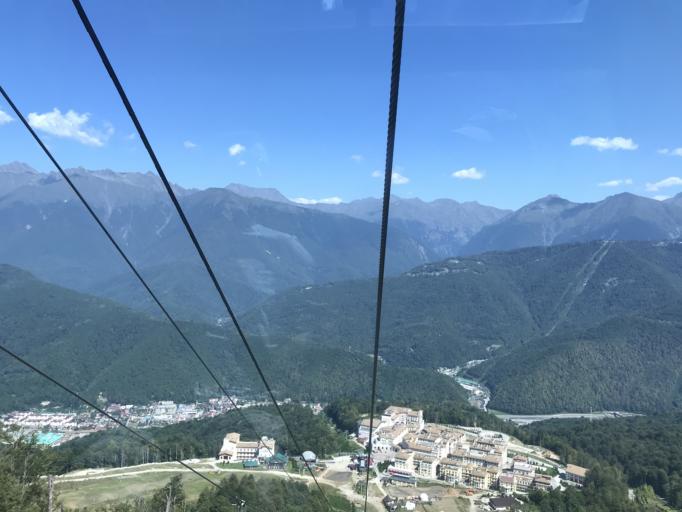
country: RU
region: Krasnodarskiy
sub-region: Sochi City
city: Krasnaya Polyana
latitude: 43.6628
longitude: 40.2539
